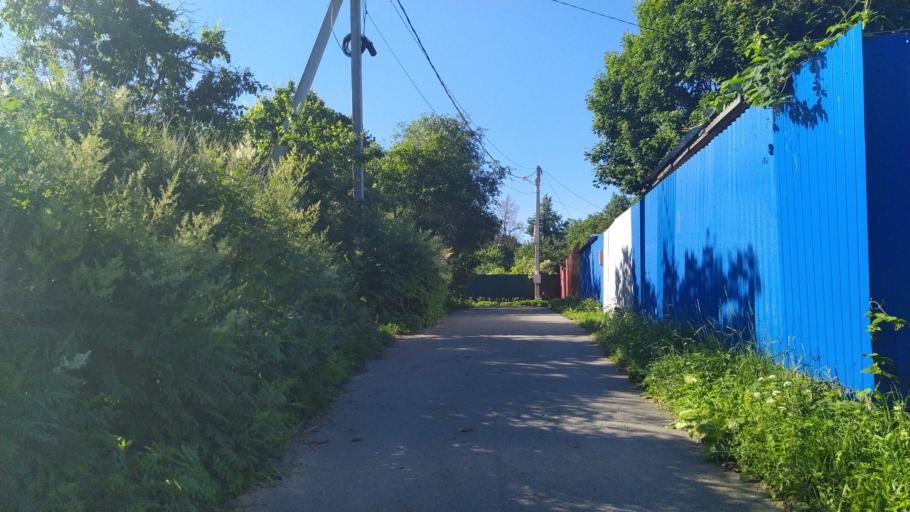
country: RU
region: Leningrad
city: Murino
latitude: 60.0459
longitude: 30.4557
